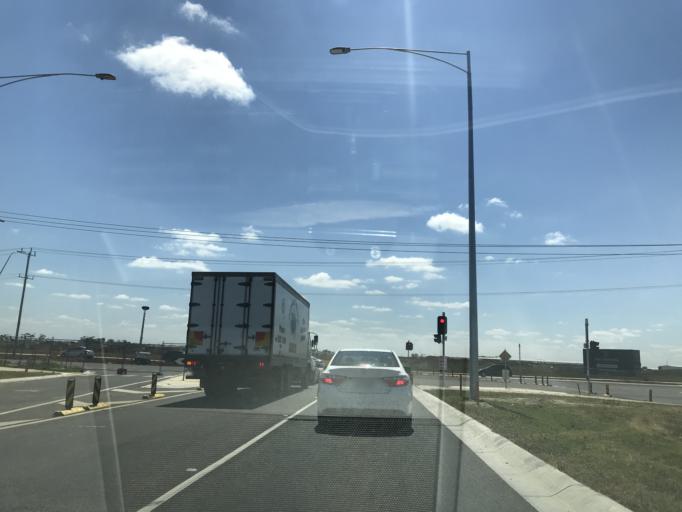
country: AU
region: Victoria
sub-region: Wyndham
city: Williams Landing
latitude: -37.8386
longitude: 144.7314
